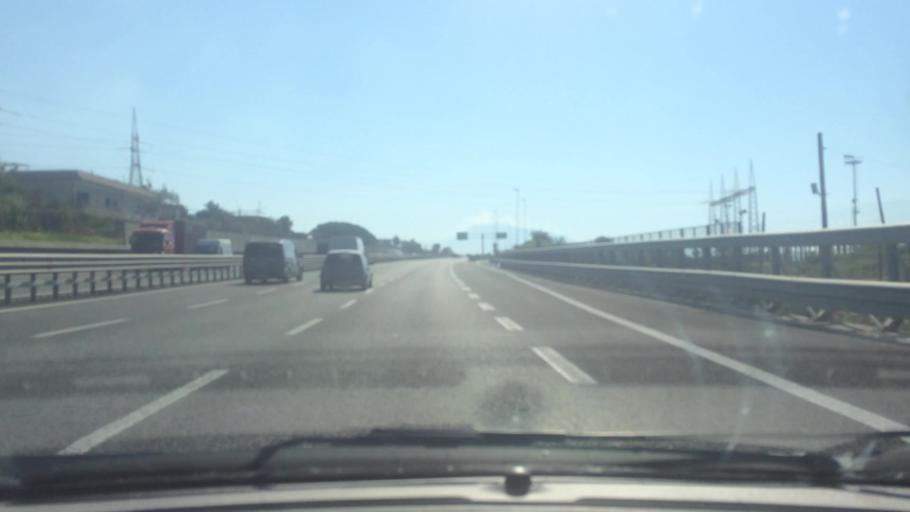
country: IT
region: Campania
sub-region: Provincia di Napoli
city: Ercolano
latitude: 40.8097
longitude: 14.3622
